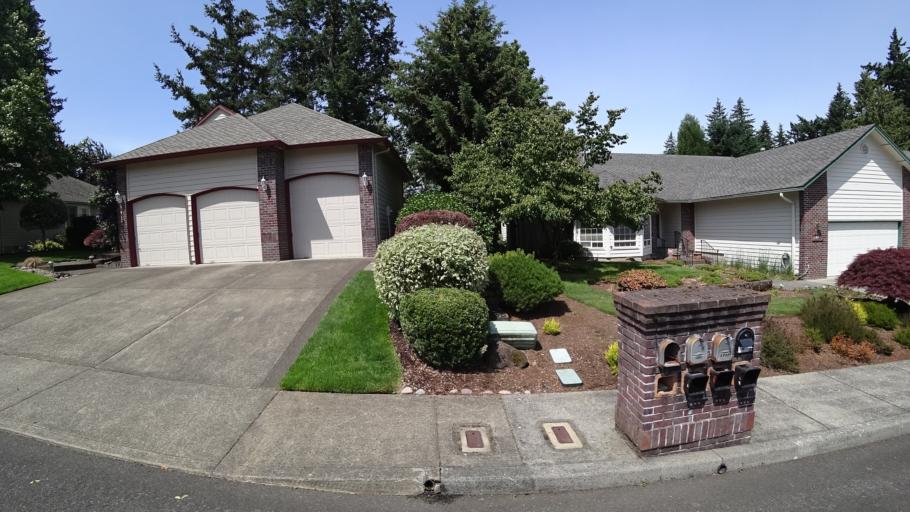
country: US
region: Oregon
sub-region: Multnomah County
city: Fairview
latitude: 45.5440
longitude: -122.5039
